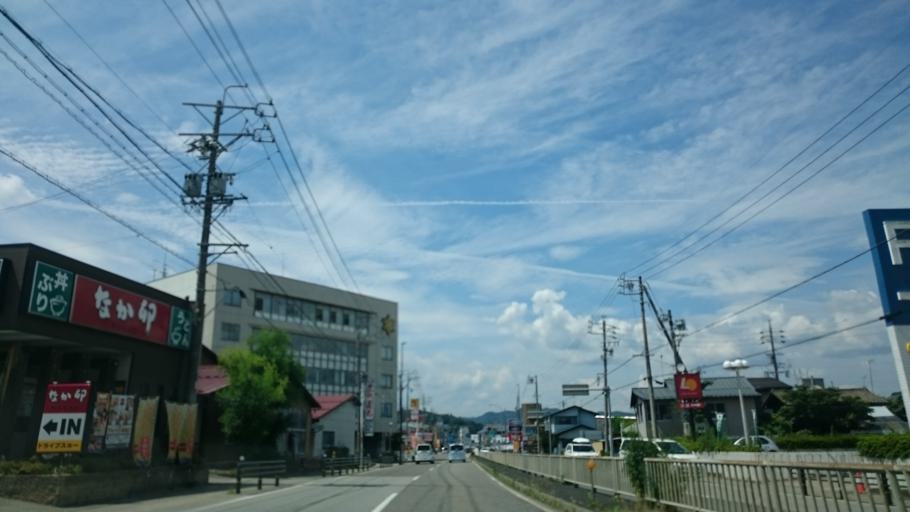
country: JP
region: Gifu
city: Takayama
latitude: 36.1327
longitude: 137.2476
